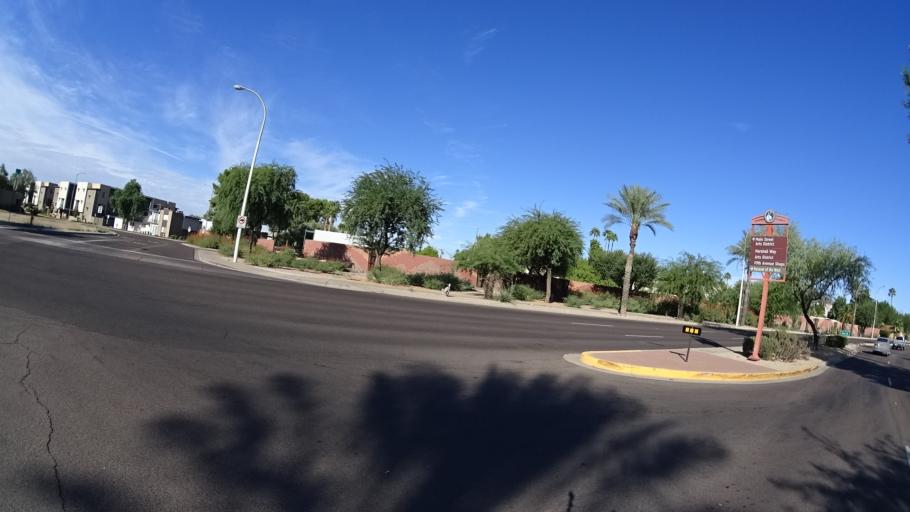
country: US
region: Arizona
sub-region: Maricopa County
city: Scottsdale
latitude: 33.4902
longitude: -111.9298
